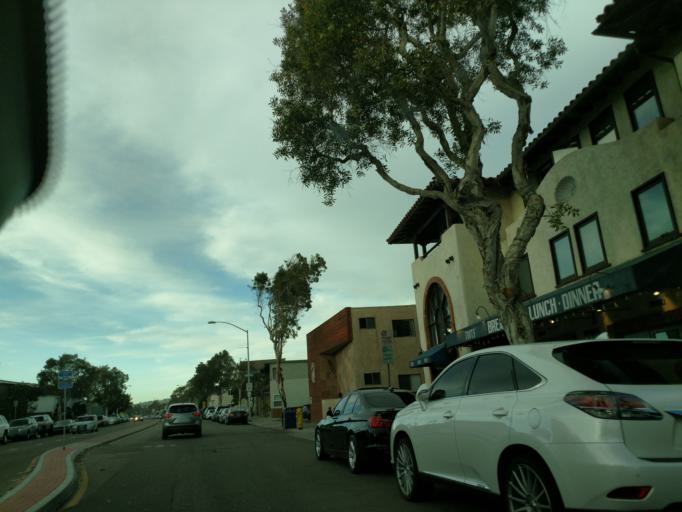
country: US
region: California
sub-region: San Diego County
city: La Jolla
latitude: 32.7726
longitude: -117.2513
